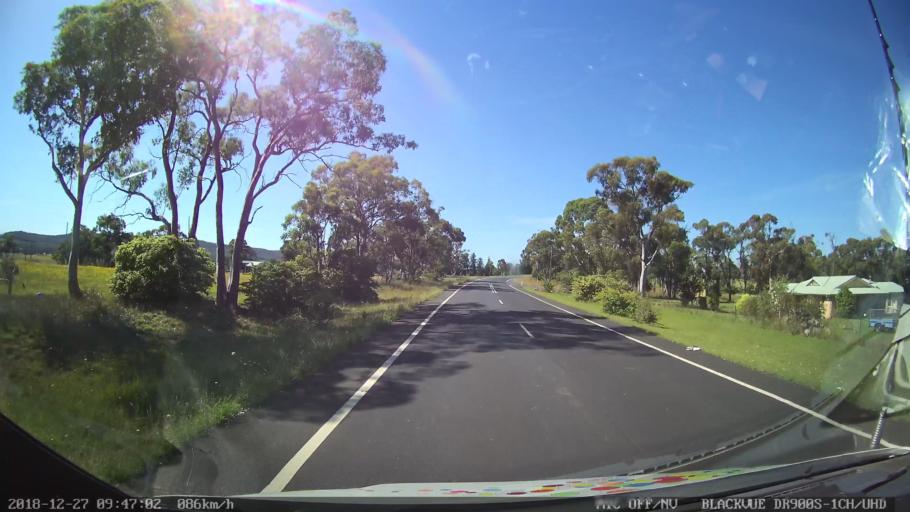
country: AU
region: New South Wales
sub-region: Lithgow
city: Portland
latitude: -33.3418
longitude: 149.9885
